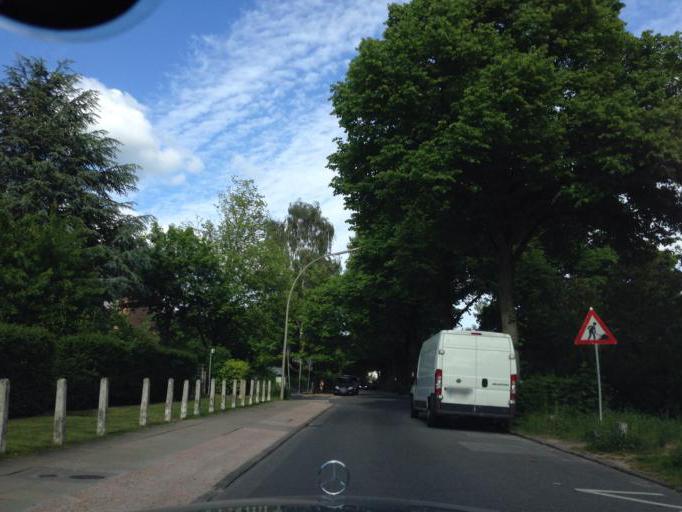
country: DE
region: Hamburg
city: Farmsen-Berne
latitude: 53.6038
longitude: 10.1365
